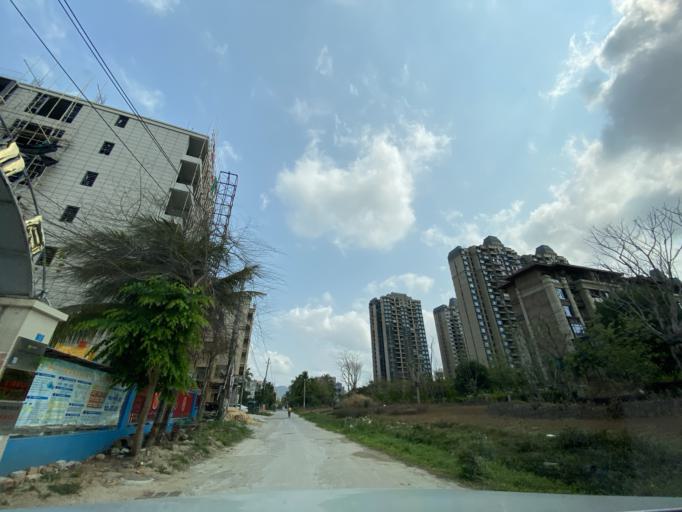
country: CN
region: Hainan
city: Yingzhou
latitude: 18.4170
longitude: 109.8488
